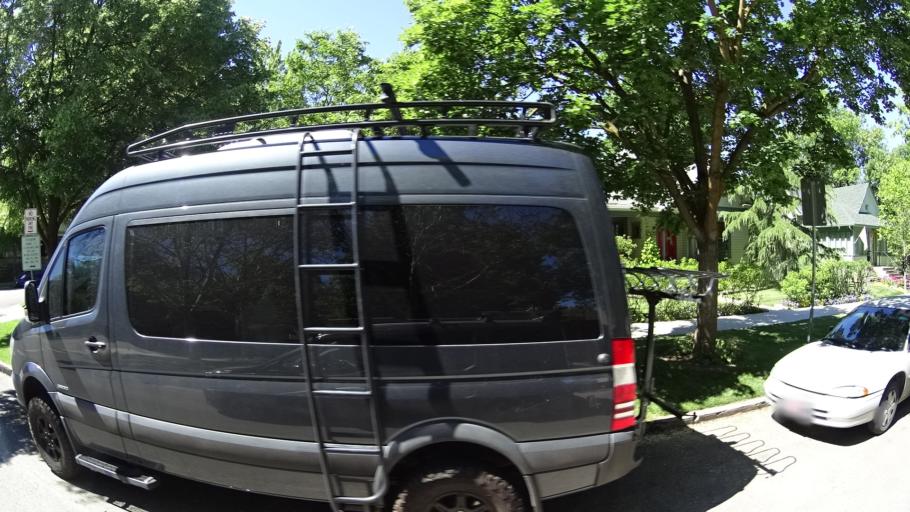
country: US
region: Idaho
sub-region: Ada County
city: Boise
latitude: 43.6231
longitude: -116.2004
